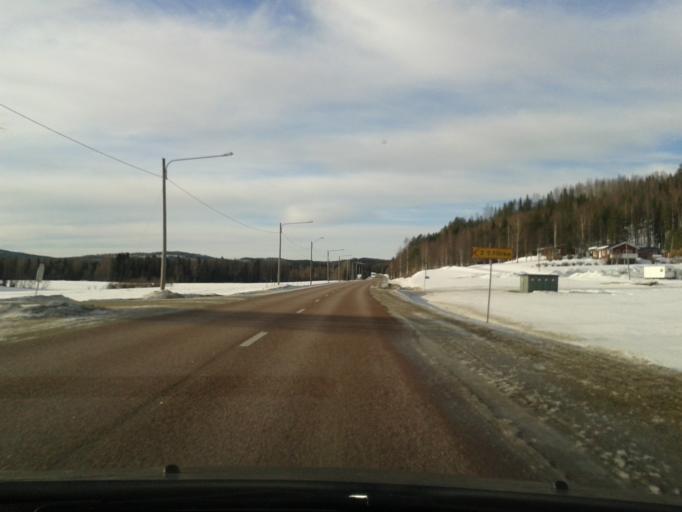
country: SE
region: Vaesternorrland
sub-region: OErnskoeldsviks Kommun
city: Bredbyn
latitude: 63.3907
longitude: 18.3455
